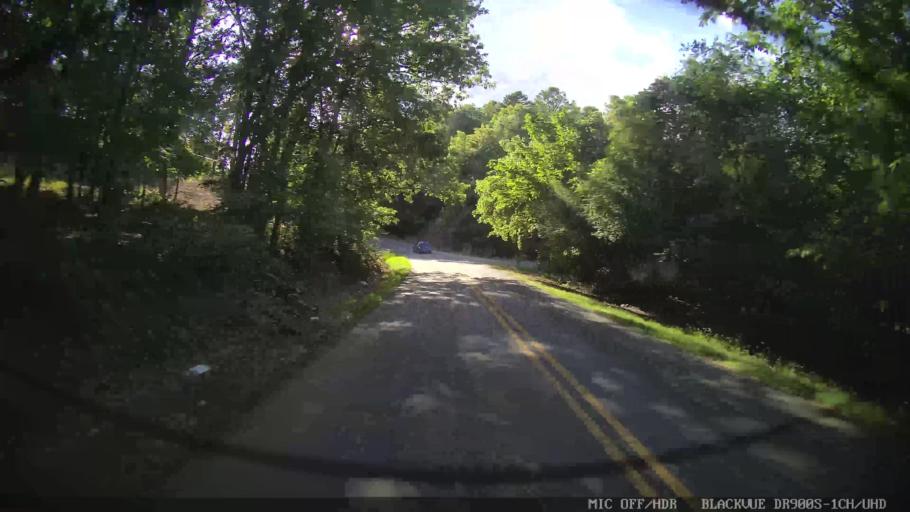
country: US
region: Georgia
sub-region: Floyd County
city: Rome
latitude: 34.2328
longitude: -85.1463
